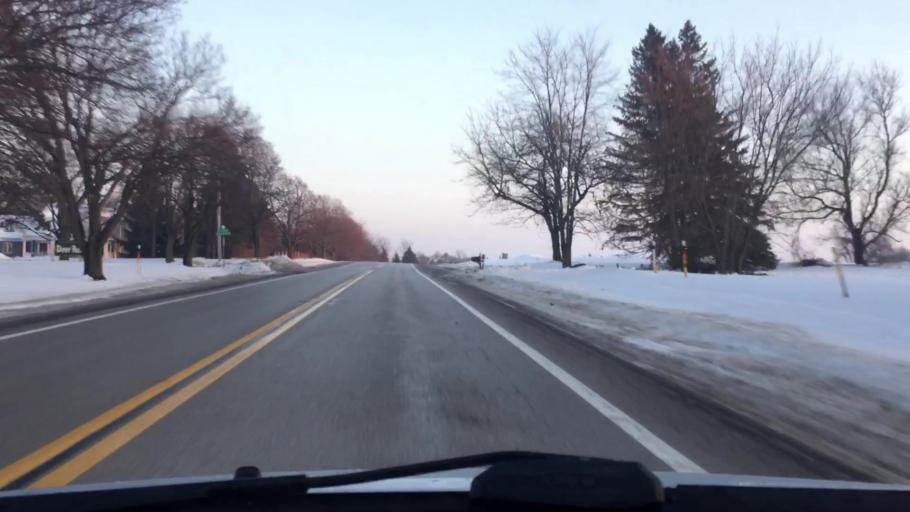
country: US
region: Illinois
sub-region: Kane County
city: Wasco
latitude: 41.9457
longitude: -88.4020
